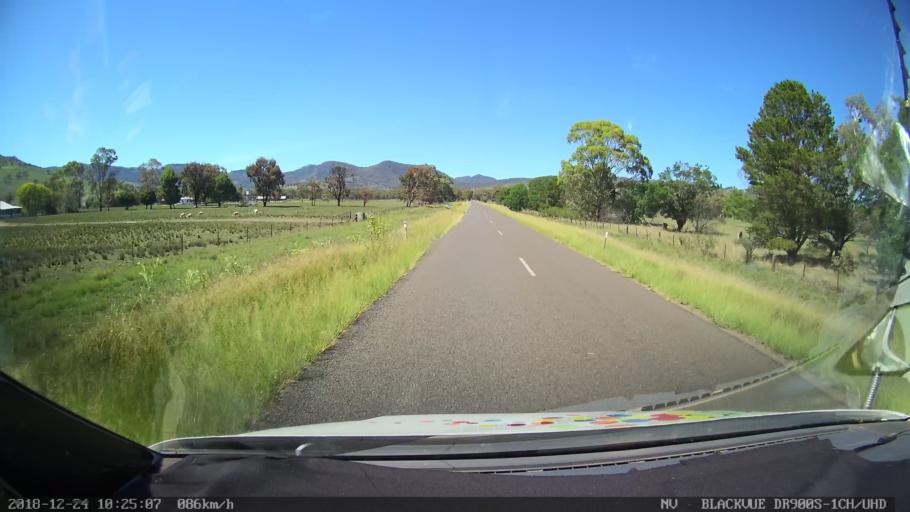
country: AU
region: New South Wales
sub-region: Liverpool Plains
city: Quirindi
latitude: -31.7949
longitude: 150.5299
